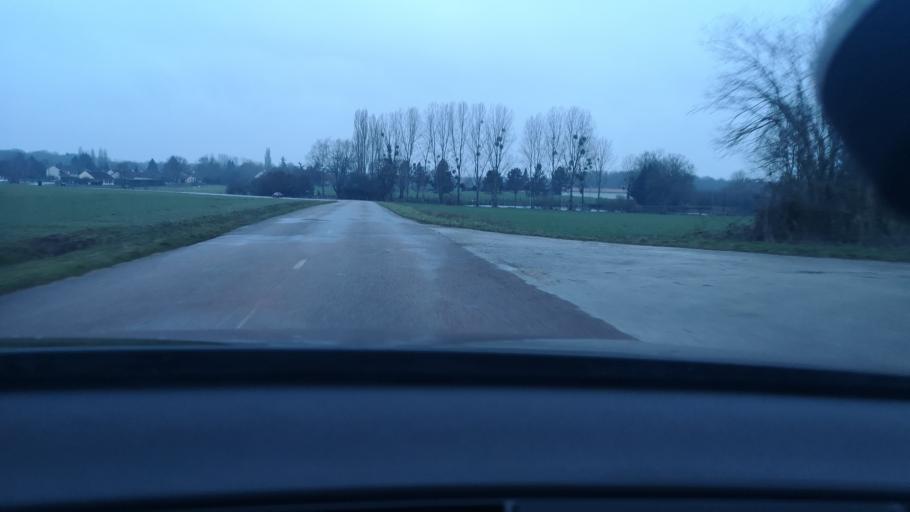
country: FR
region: Bourgogne
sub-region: Departement de la Cote-d'Or
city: Seurre
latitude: 47.0330
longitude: 5.0664
